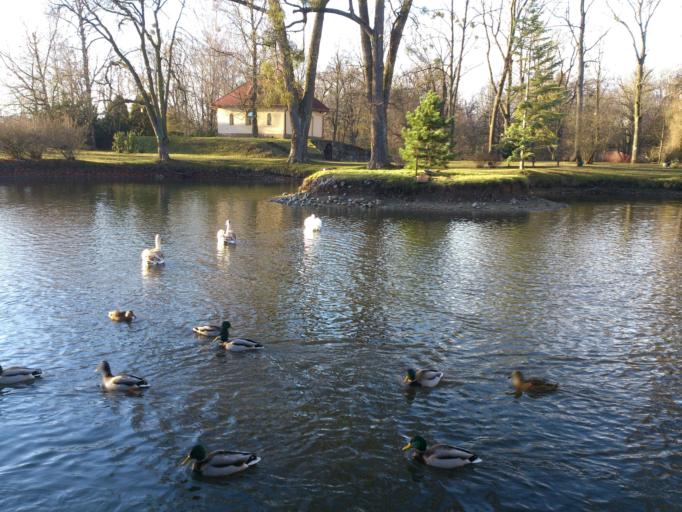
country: LT
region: Kauno apskritis
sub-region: Kaunas
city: Aleksotas
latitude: 54.8710
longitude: 23.9116
